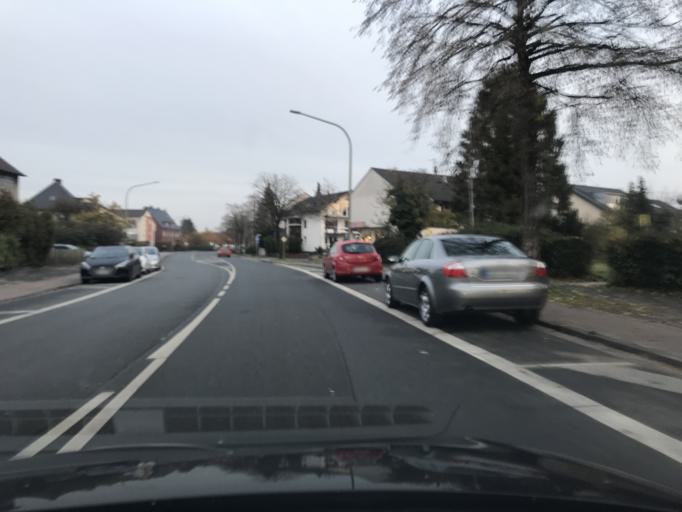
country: DE
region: North Rhine-Westphalia
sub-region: Regierungsbezirk Arnsberg
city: Hamm
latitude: 51.6911
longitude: 7.8630
